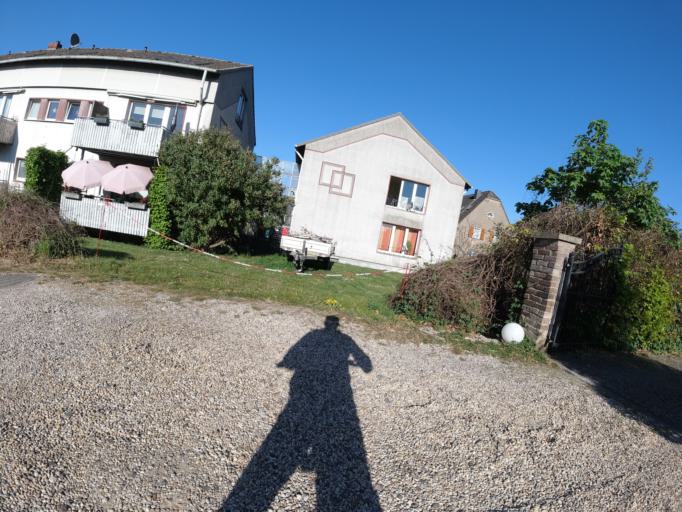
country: DE
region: North Rhine-Westphalia
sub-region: Regierungsbezirk Dusseldorf
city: Hochfeld
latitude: 51.3823
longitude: 6.7053
